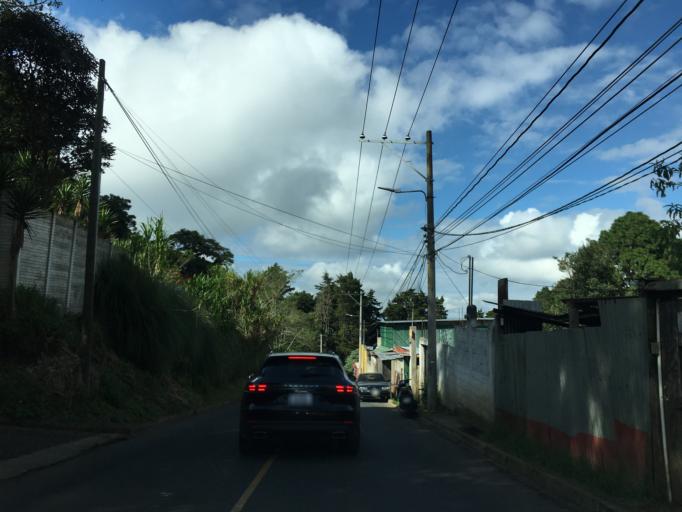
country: GT
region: Guatemala
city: San Jose Pinula
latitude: 14.5690
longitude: -90.4401
